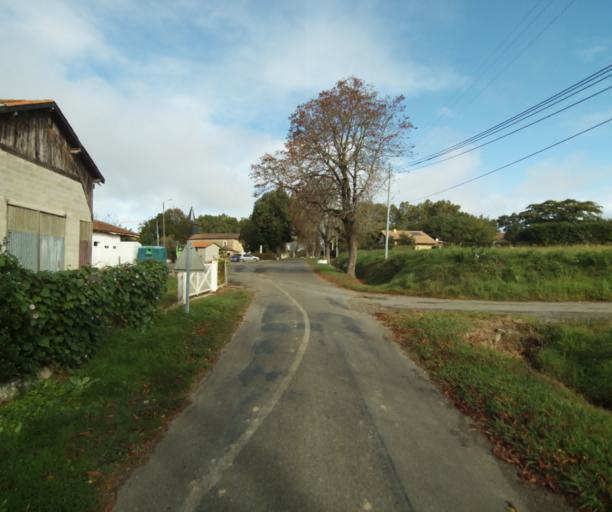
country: FR
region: Midi-Pyrenees
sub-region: Departement du Gers
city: Cazaubon
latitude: 43.8636
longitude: -0.0726
